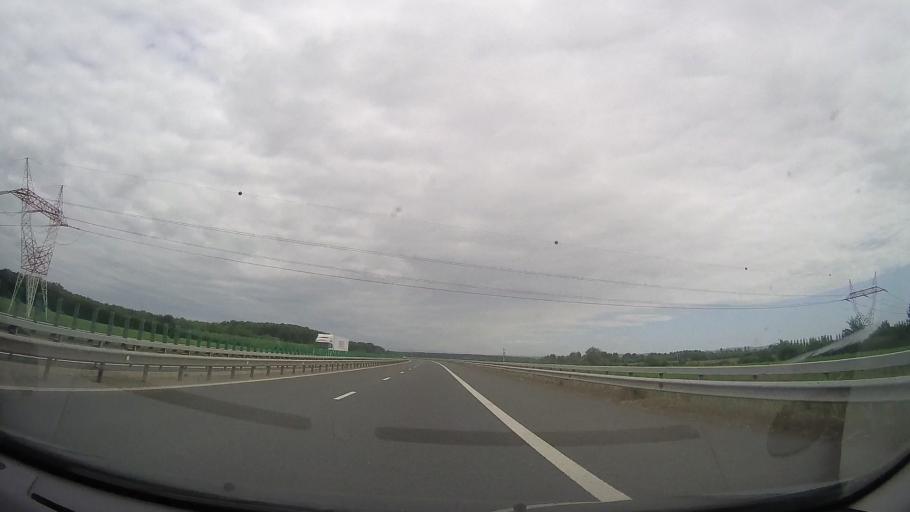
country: RO
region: Prahova
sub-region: Comuna Rafov
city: Rafov
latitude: 44.8785
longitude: 26.1364
